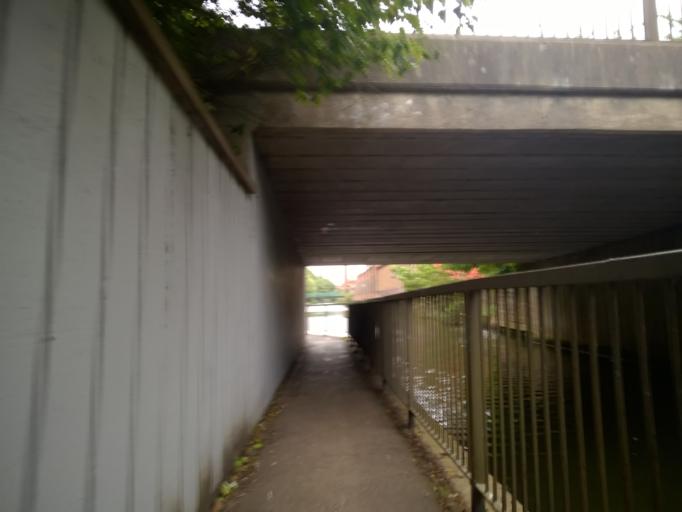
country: GB
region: England
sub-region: City of Leicester
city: Leicester
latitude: 52.6421
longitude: -1.1390
